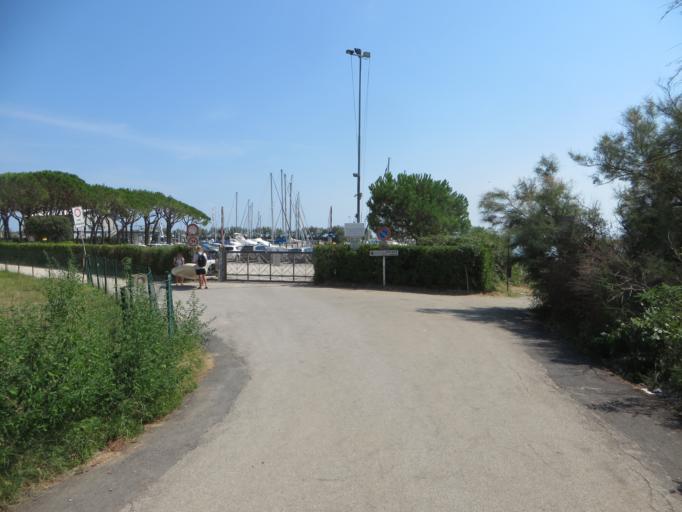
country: IT
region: Veneto
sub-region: Provincia di Venezia
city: Crepaldo
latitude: 45.5429
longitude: 12.7536
